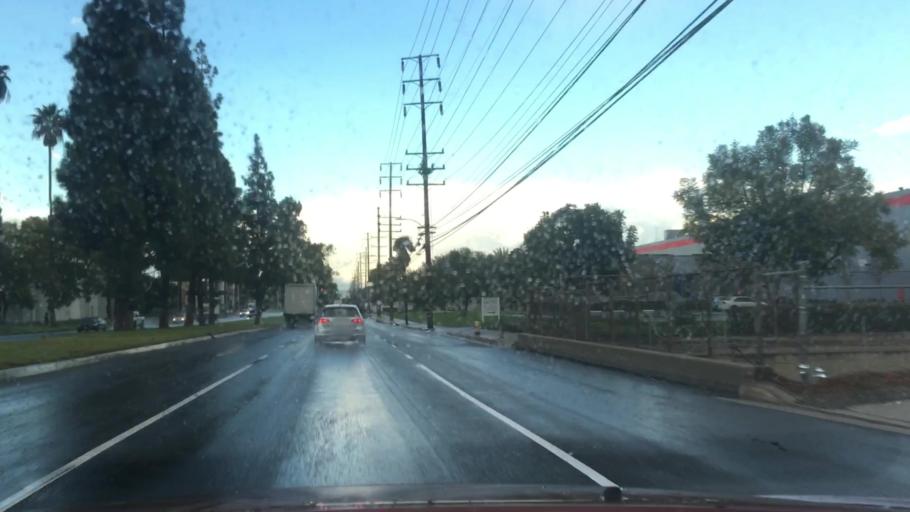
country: US
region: California
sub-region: Orange County
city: La Palma
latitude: 33.8640
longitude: -118.0286
